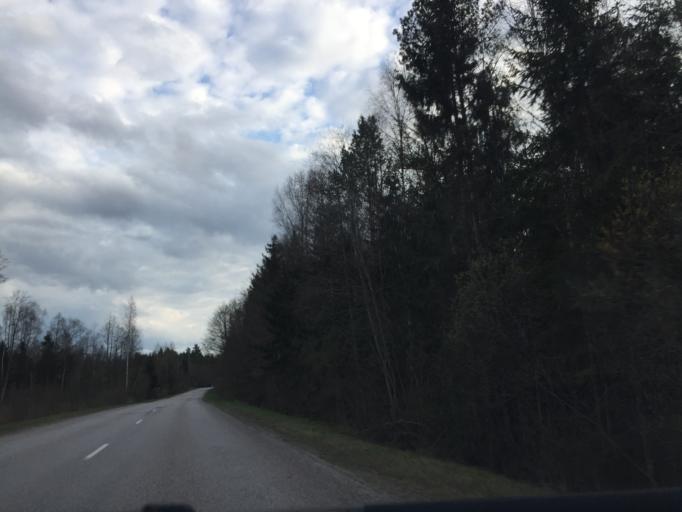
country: LV
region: Aluksnes Rajons
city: Aluksne
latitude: 57.3076
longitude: 27.0712
